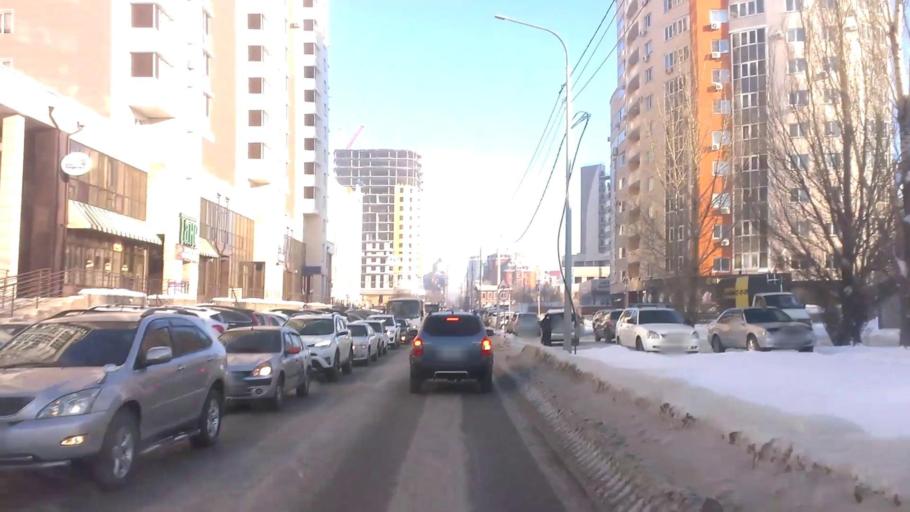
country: RU
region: Altai Krai
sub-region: Gorod Barnaulskiy
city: Barnaul
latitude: 53.3368
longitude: 83.7779
